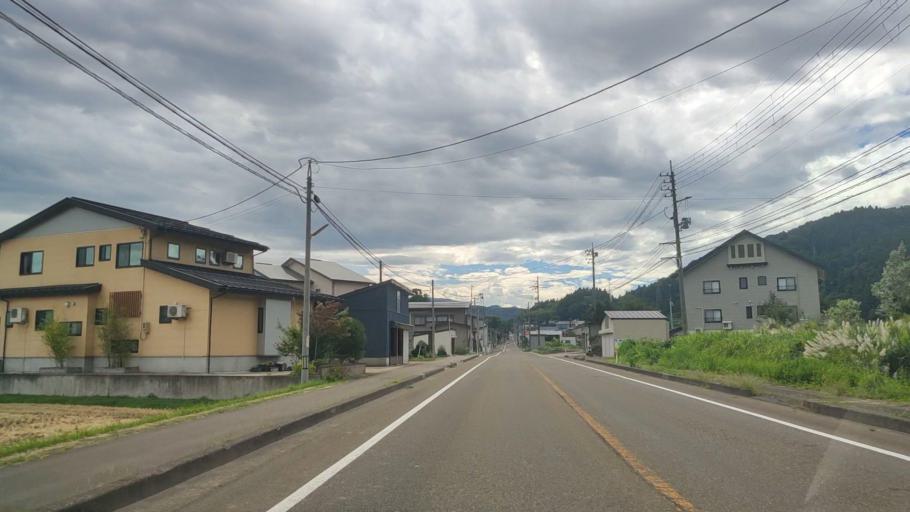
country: JP
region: Niigata
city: Arai
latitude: 37.0041
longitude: 138.2628
